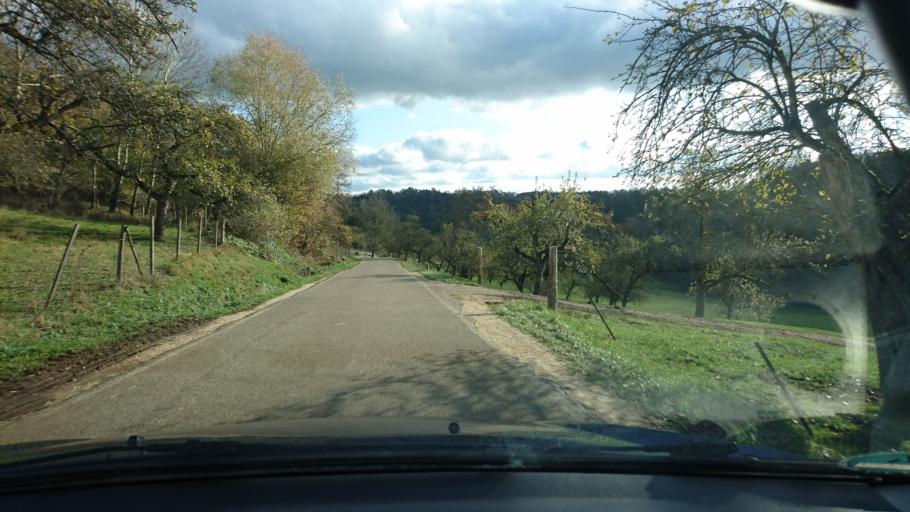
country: DE
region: Baden-Wuerttemberg
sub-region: Regierungsbezirk Stuttgart
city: Heuchlingen
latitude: 48.8783
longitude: 9.9664
